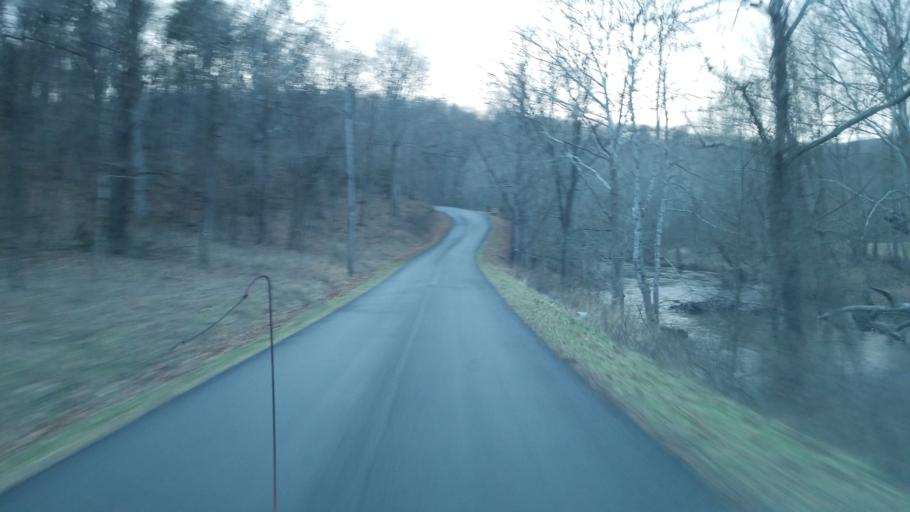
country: US
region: Virginia
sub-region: Pulaski County
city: Pulaski
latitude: 37.1522
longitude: -80.8697
